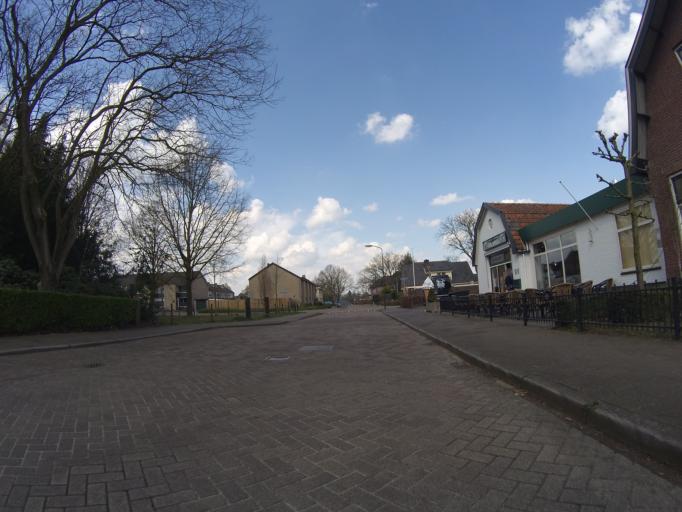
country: NL
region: Gelderland
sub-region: Gemeente Barneveld
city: Terschuur
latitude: 52.1380
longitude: 5.4968
